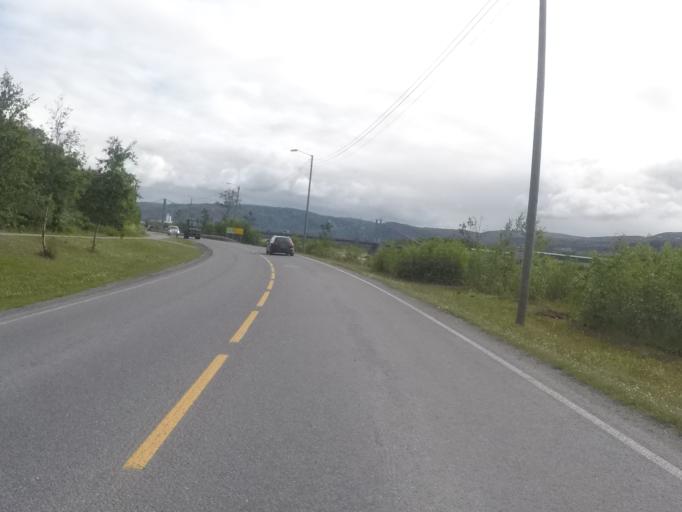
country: NO
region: Finnmark Fylke
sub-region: Alta
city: Alta
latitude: 69.9676
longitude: 23.3679
